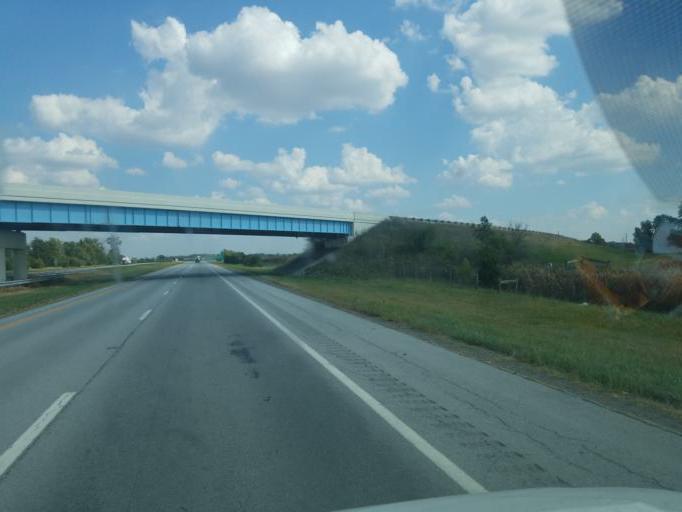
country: US
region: Ohio
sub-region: Allen County
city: Delphos
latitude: 40.8733
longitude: -84.3650
